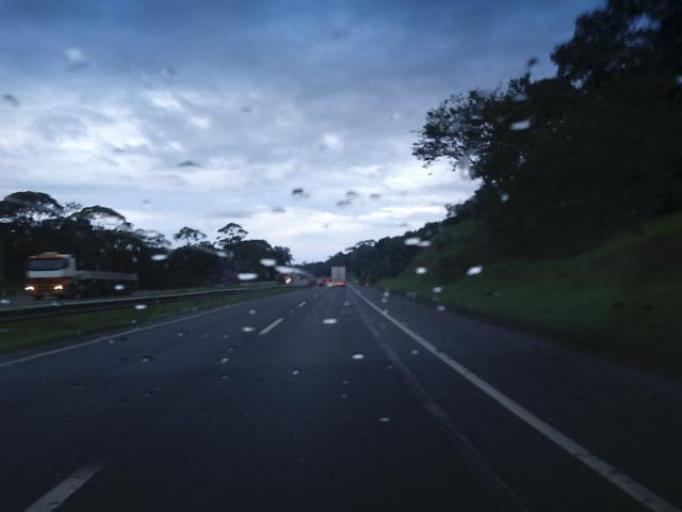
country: BR
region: Santa Catarina
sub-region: Joinville
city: Joinville
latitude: -26.0153
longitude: -48.8620
